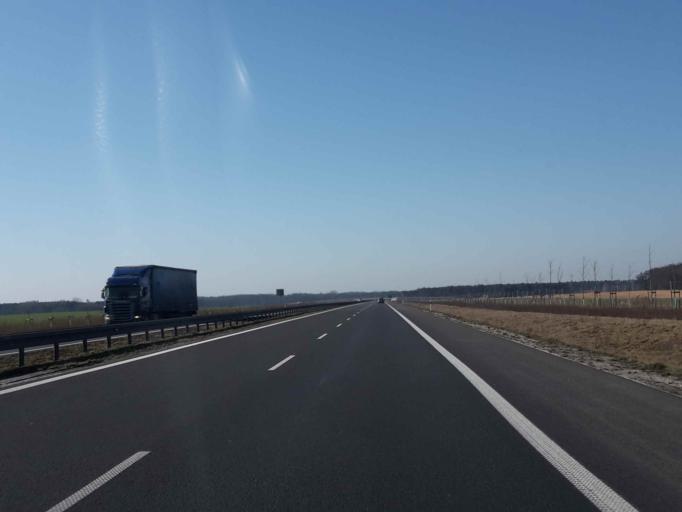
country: PL
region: Greater Poland Voivodeship
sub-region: Powiat poznanski
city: Pobiedziska
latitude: 52.4212
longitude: 17.3015
